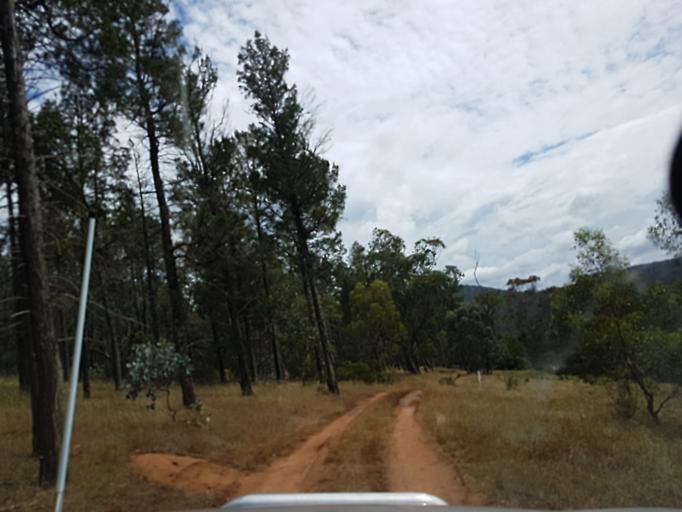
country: AU
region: New South Wales
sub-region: Snowy River
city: Jindabyne
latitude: -36.9345
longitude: 148.4001
